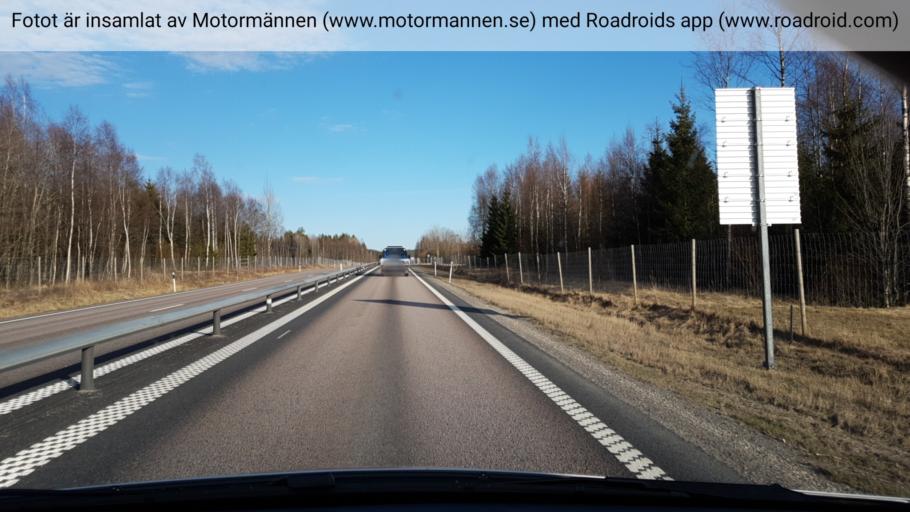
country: SE
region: Vaesternorrland
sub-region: OErnskoeldsviks Kommun
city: Ornskoldsvik
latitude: 63.3067
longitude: 18.8479
